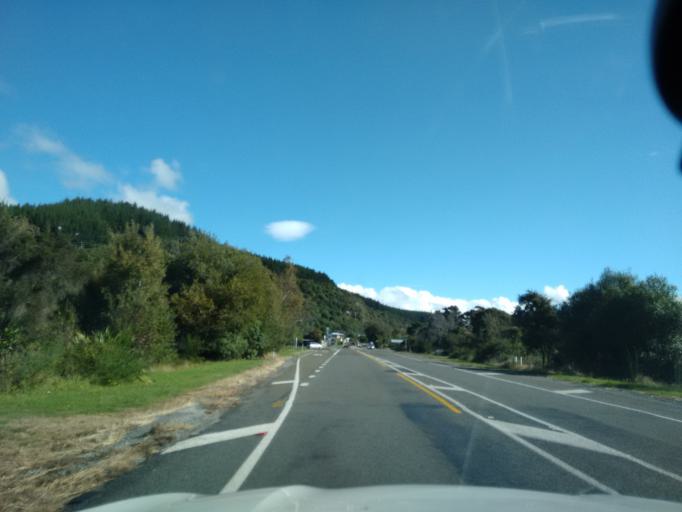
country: NZ
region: Waikato
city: Turangi
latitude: -38.9303
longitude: 175.8777
